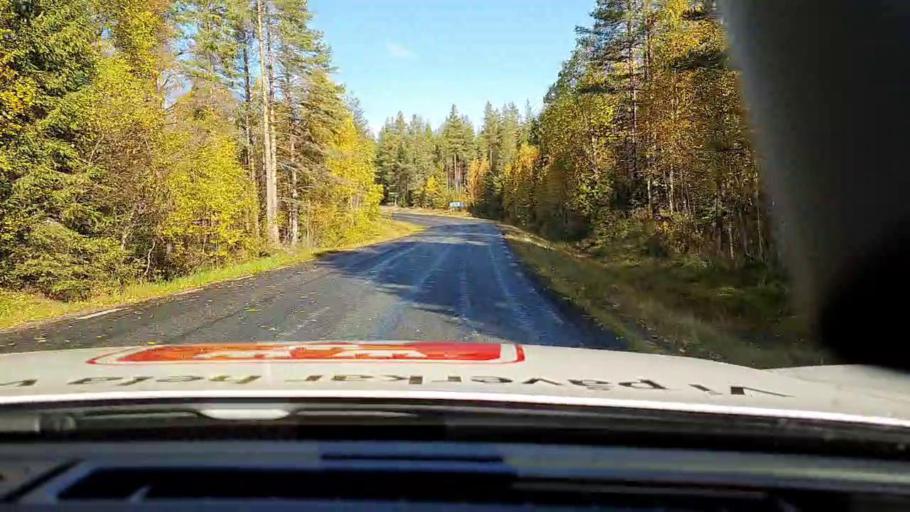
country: SE
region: Vaesterbotten
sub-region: Skelleftea Kommun
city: Langsele
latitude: 65.0010
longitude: 20.0908
